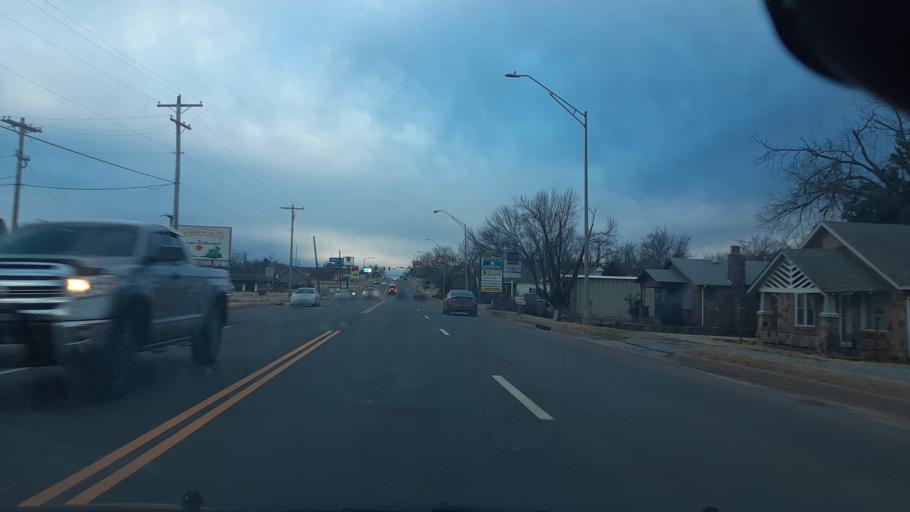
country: US
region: Oklahoma
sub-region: Logan County
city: Guthrie
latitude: 35.8650
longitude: -97.4254
